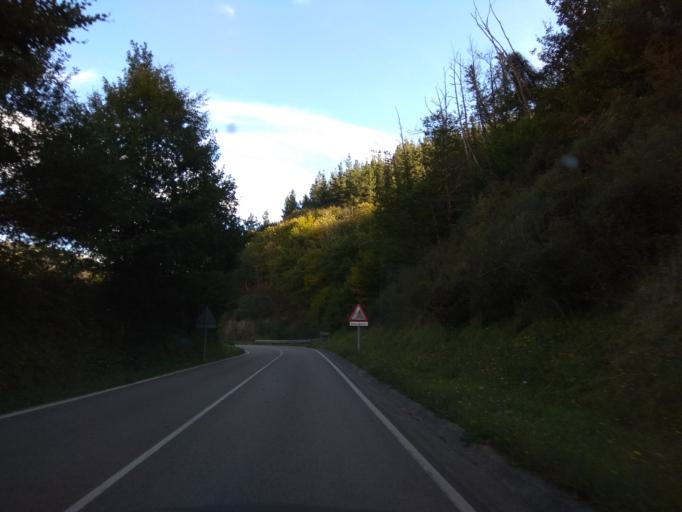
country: ES
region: Cantabria
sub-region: Provincia de Cantabria
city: Ruente
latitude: 43.2132
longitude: -4.3759
